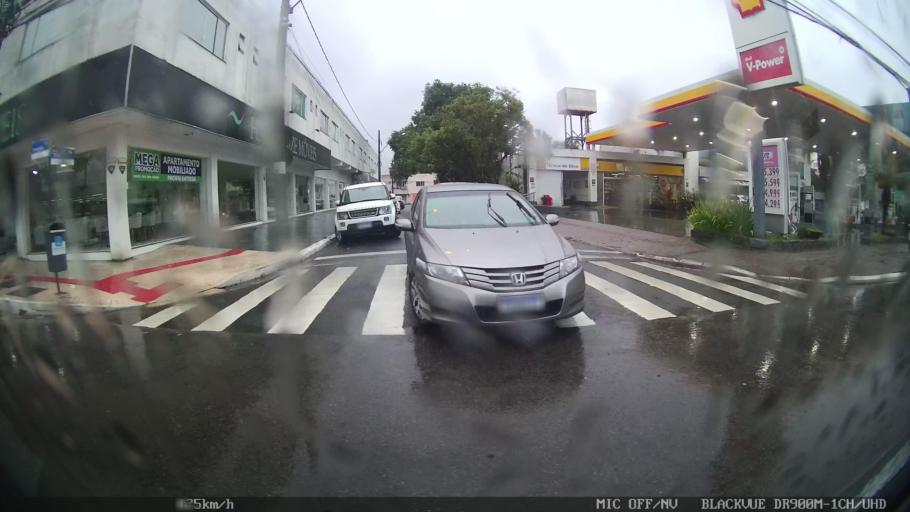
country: BR
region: Santa Catarina
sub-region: Balneario Camboriu
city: Balneario Camboriu
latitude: -26.9963
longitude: -48.6398
